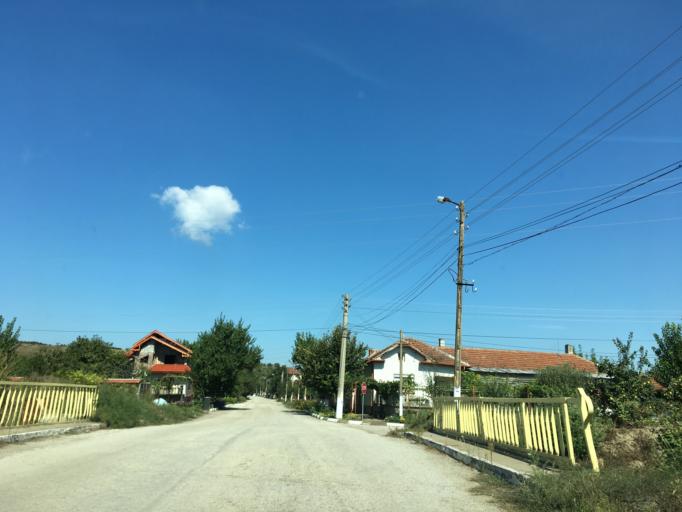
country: RO
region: Olt
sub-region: Comuna Orlea
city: Orlea
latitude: 43.6440
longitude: 24.3999
